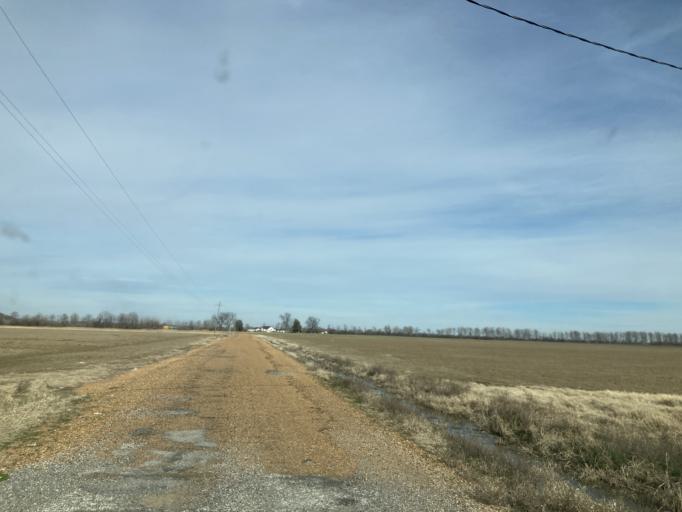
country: US
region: Mississippi
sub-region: Humphreys County
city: Belzoni
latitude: 33.0637
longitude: -90.6335
